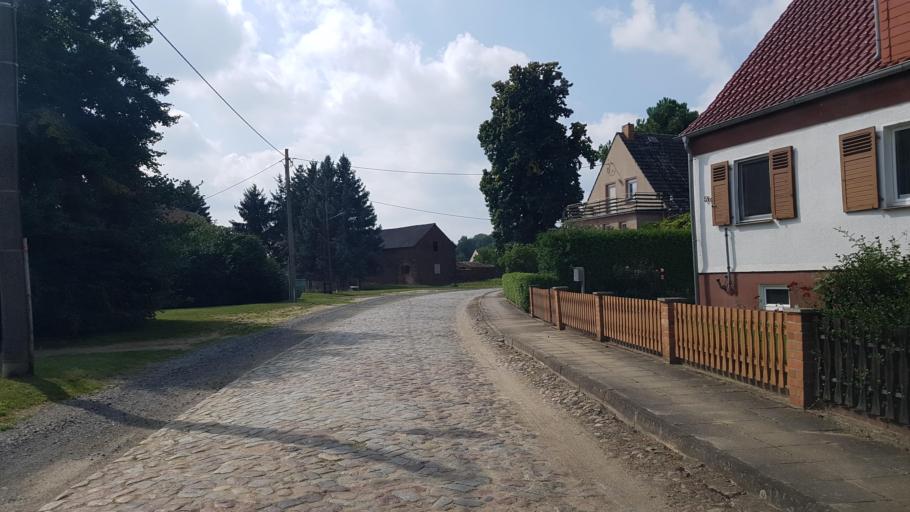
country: DE
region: Brandenburg
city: Luckau
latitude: 51.8215
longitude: 13.6546
